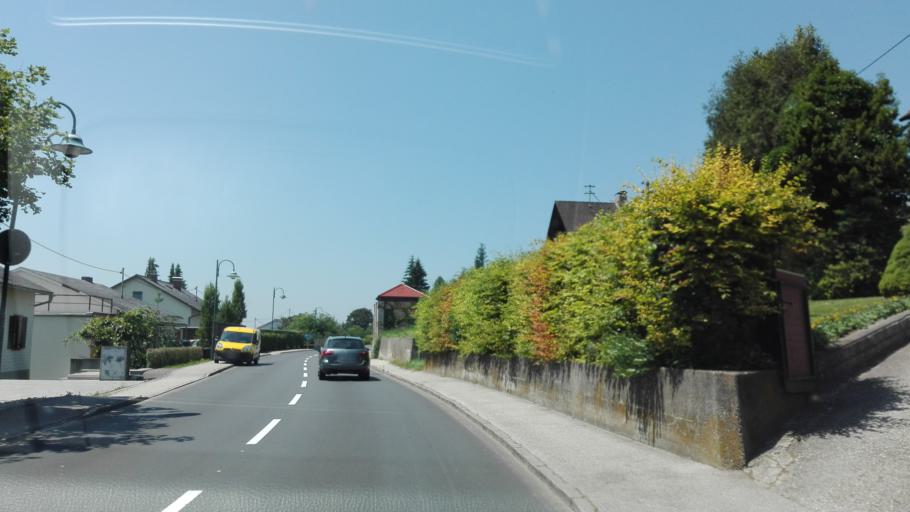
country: AT
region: Upper Austria
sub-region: Politischer Bezirk Linz-Land
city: Pasching
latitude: 48.2821
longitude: 14.1554
